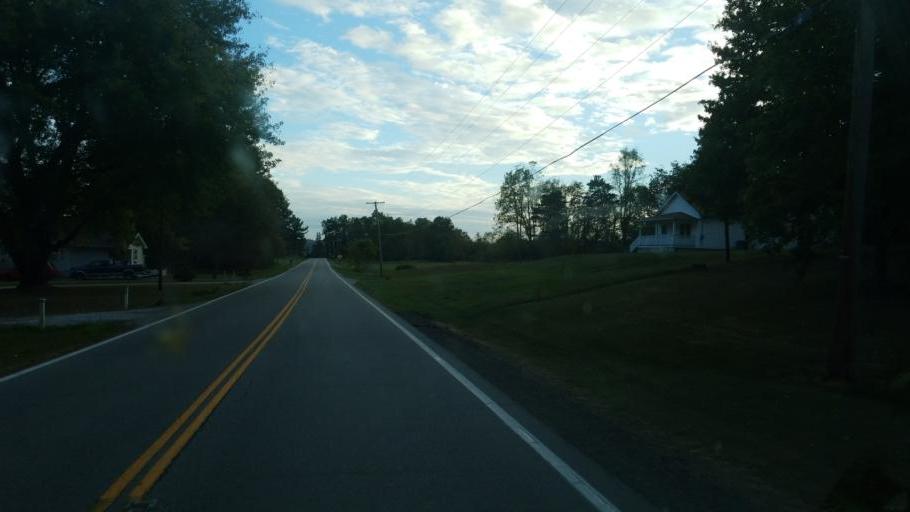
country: US
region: Ohio
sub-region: Ashland County
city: Loudonville
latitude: 40.6491
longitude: -82.2296
